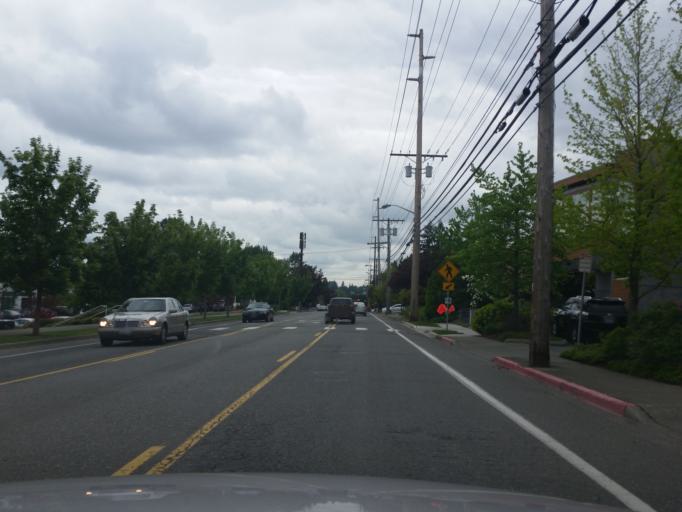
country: US
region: Washington
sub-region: King County
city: Kirkland
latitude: 47.6694
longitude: -122.1963
